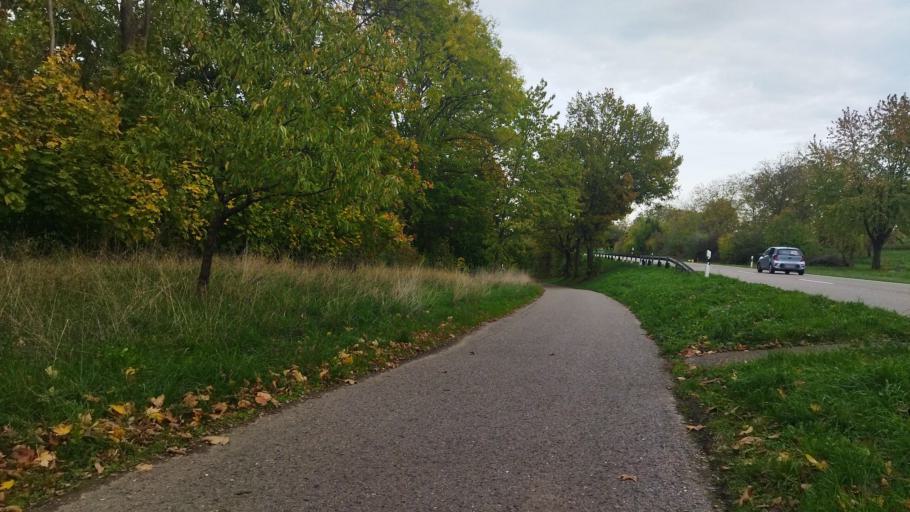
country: DE
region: Baden-Wuerttemberg
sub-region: Regierungsbezirk Stuttgart
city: Gemmrigheim
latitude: 49.0342
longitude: 9.1694
